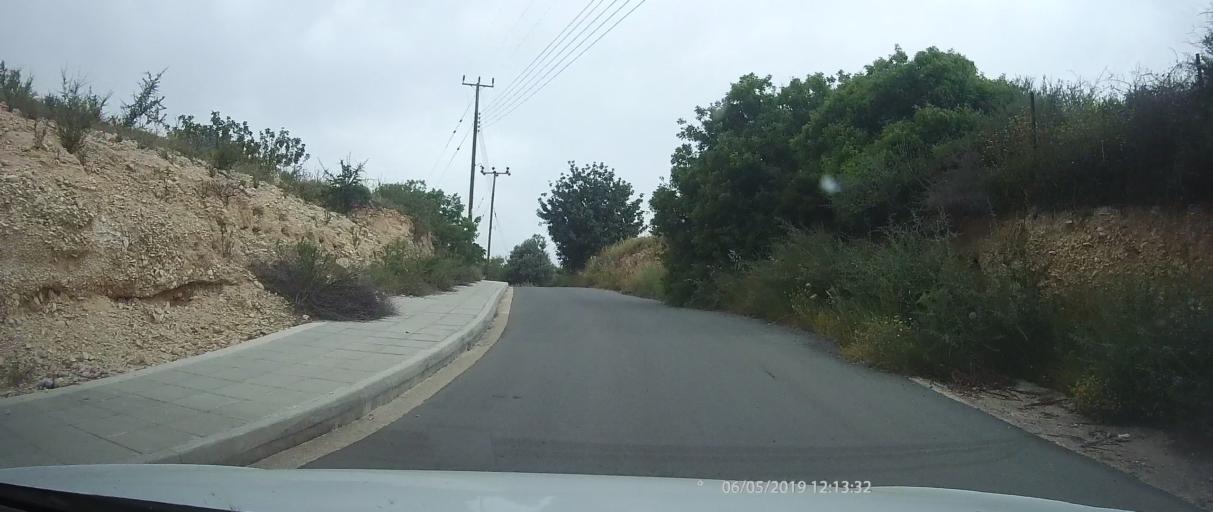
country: CY
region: Pafos
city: Tala
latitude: 34.8419
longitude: 32.4232
